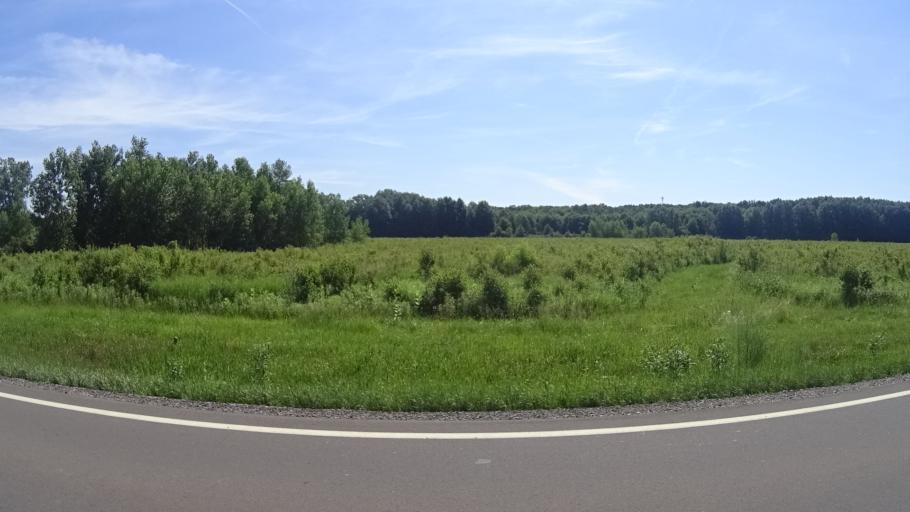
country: US
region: Ohio
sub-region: Erie County
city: Huron
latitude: 41.3457
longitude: -82.4939
